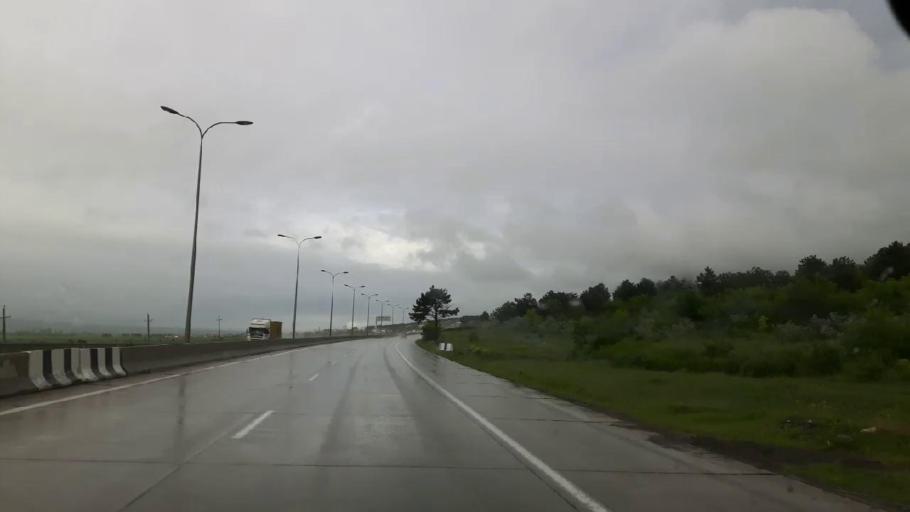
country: GE
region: Shida Kartli
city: Gori
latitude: 42.0242
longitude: 44.2184
